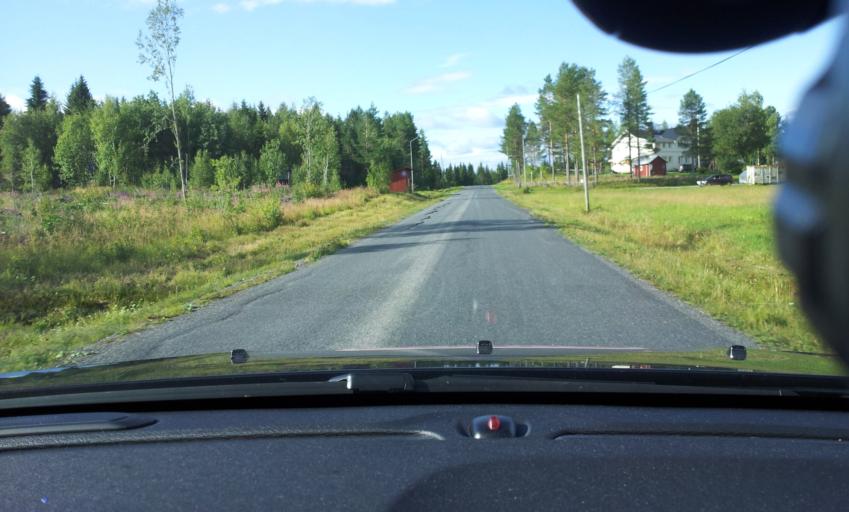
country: SE
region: Jaemtland
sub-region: Krokoms Kommun
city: Valla
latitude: 63.2739
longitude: 13.8682
